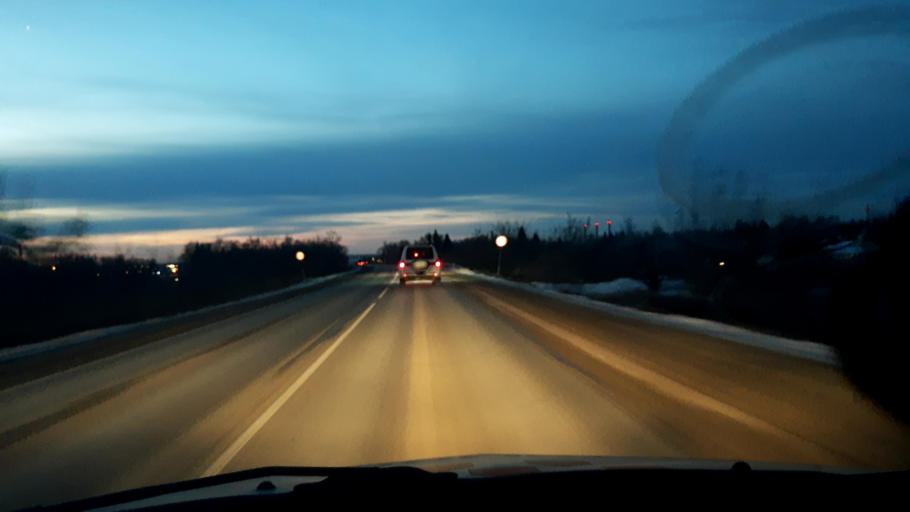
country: RU
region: Bashkortostan
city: Iglino
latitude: 54.7784
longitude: 56.2539
